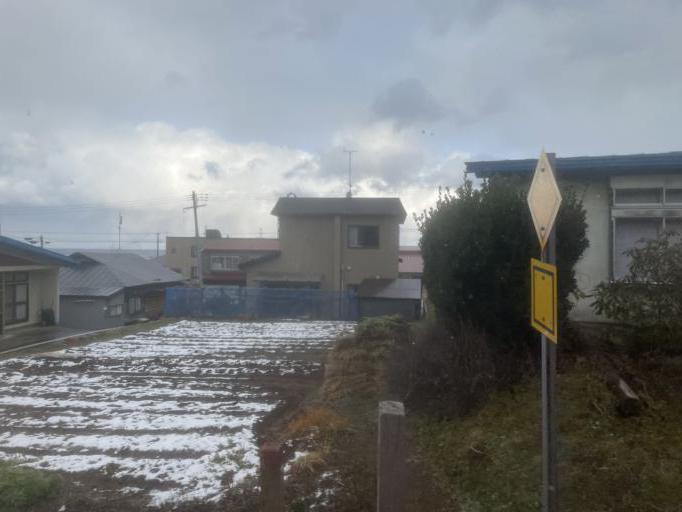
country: JP
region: Aomori
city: Shimokizukuri
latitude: 41.1810
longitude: 140.4659
